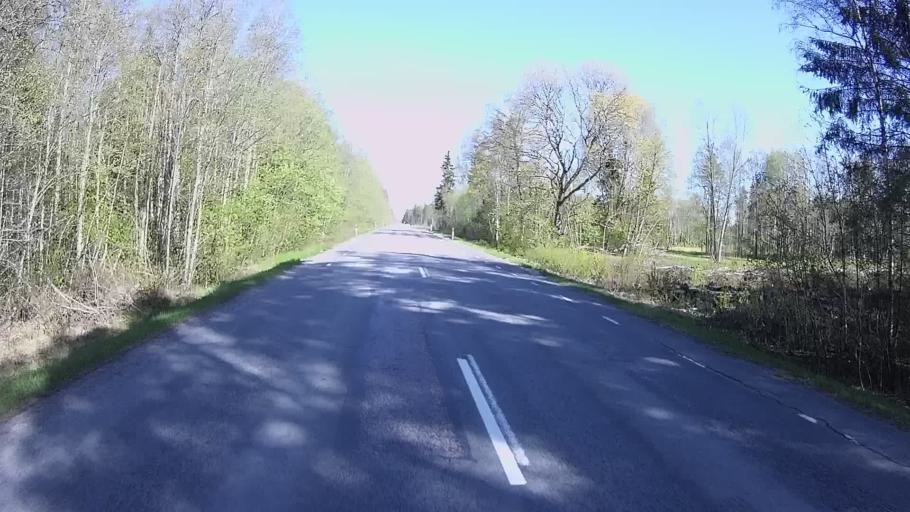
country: EE
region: Raplamaa
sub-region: Jaervakandi vald
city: Jarvakandi
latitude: 58.8527
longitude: 24.7935
